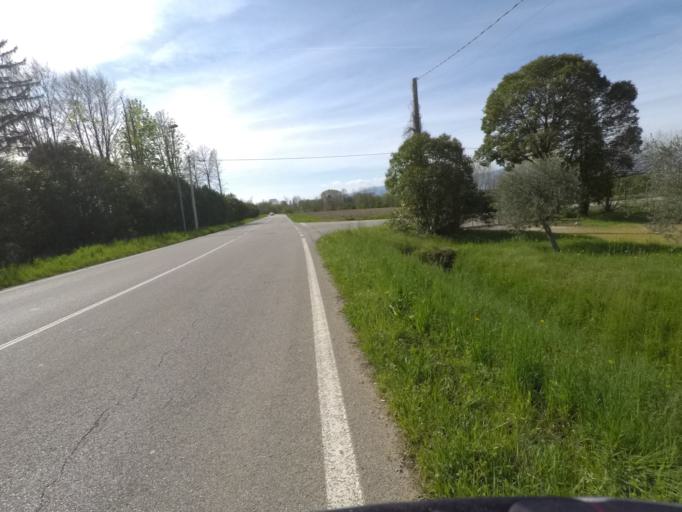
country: IT
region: Friuli Venezia Giulia
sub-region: Provincia di Pordenone
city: Fiume Veneto
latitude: 45.9362
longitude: 12.7068
